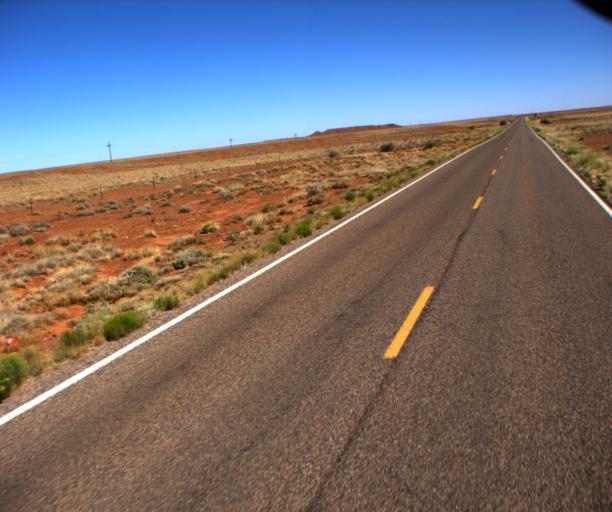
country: US
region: Arizona
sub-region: Coconino County
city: LeChee
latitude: 35.2108
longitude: -110.9498
